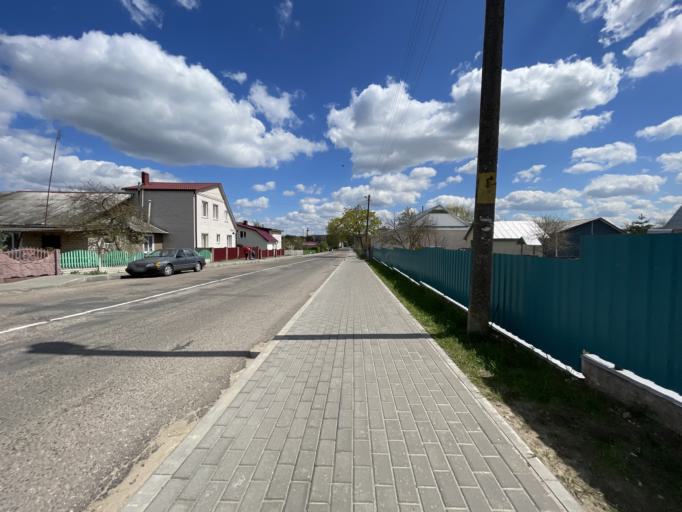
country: BY
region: Minsk
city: Nyasvizh
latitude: 53.2205
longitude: 26.6708
